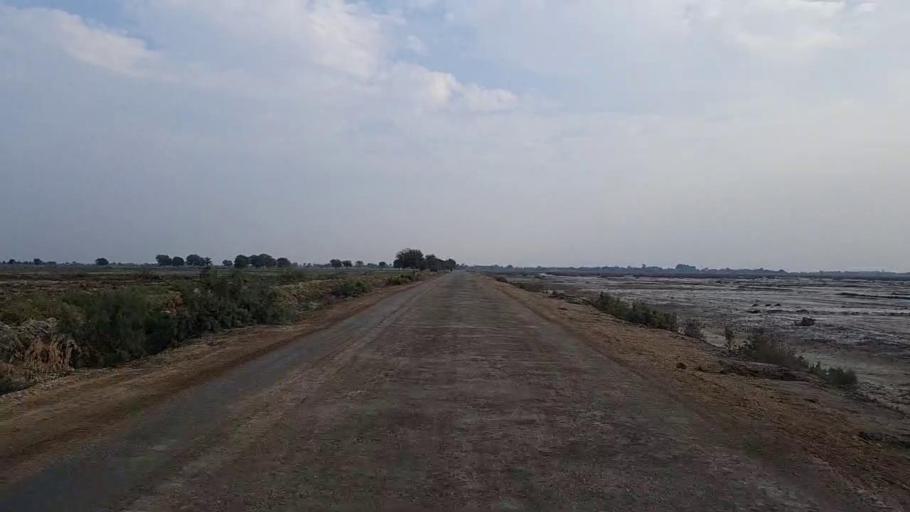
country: PK
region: Sindh
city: Pithoro
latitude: 25.4721
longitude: 69.2705
